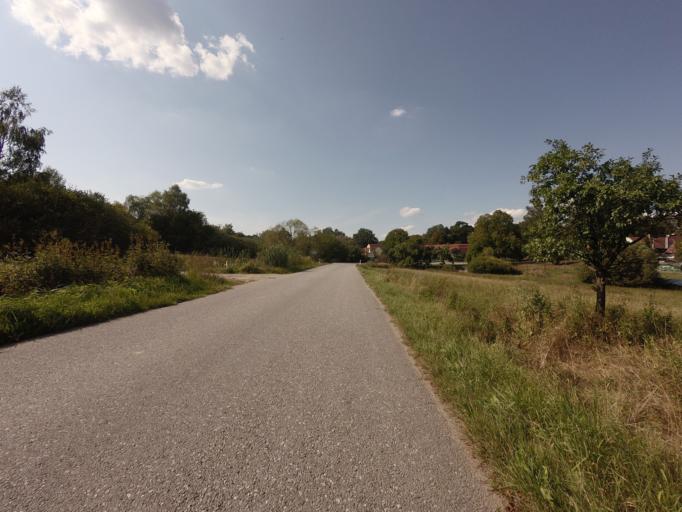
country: CZ
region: Jihocesky
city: Tyn nad Vltavou
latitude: 49.1724
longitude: 14.4205
